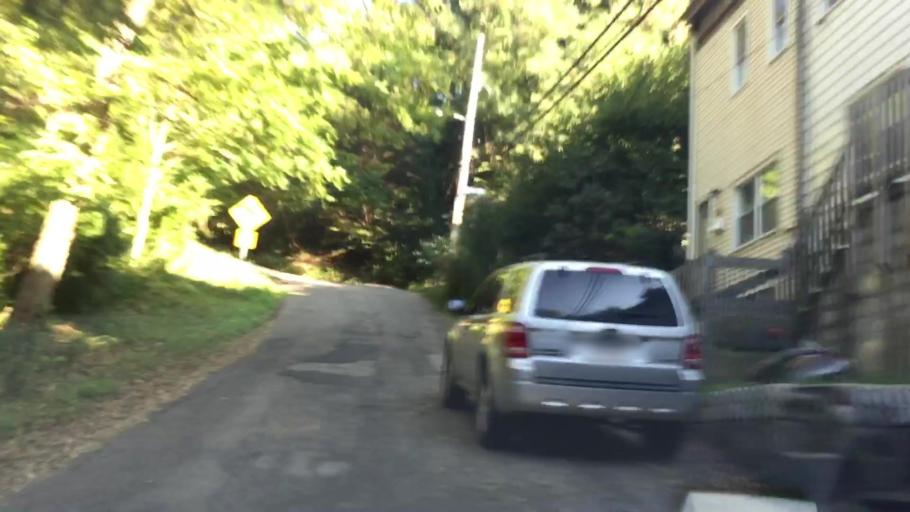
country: US
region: Pennsylvania
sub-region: Allegheny County
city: Millvale
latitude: 40.4689
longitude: -79.9971
